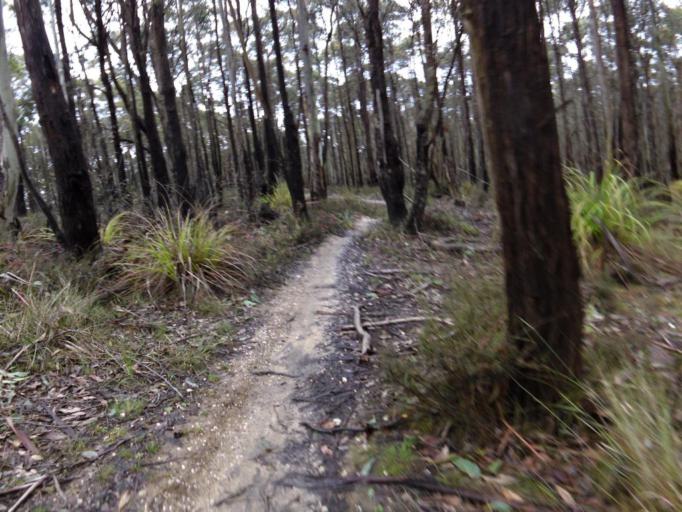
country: AU
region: Victoria
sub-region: Moorabool
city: Bacchus Marsh
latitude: -37.4184
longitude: 144.4913
